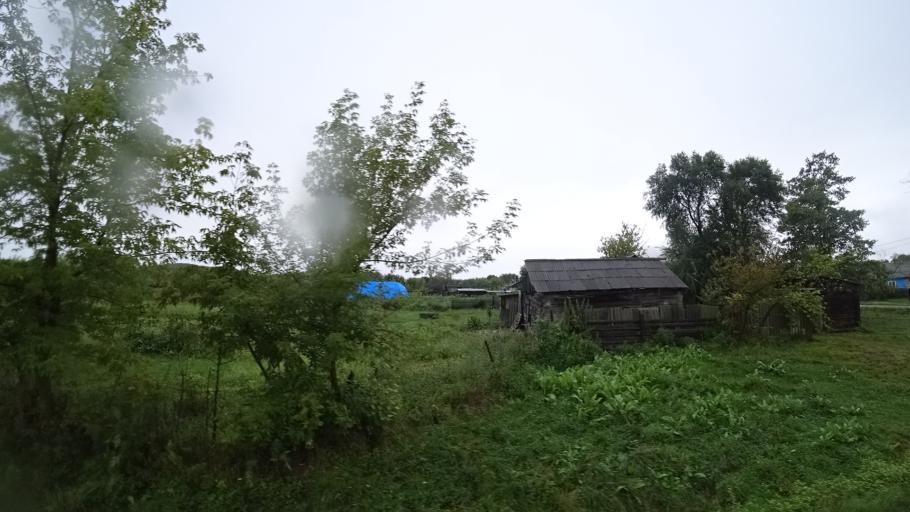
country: RU
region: Primorskiy
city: Monastyrishche
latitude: 44.2557
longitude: 132.4272
